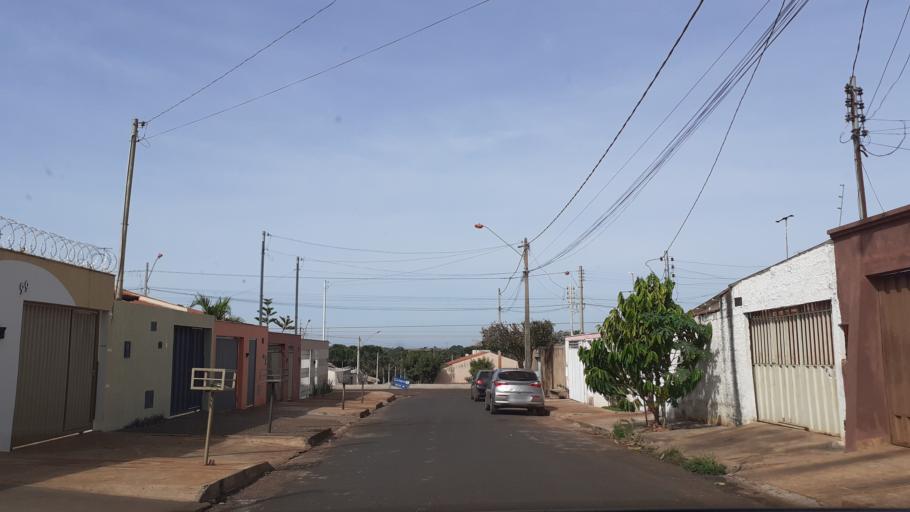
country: BR
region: Goias
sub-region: Itumbiara
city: Itumbiara
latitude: -18.4182
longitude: -49.2386
